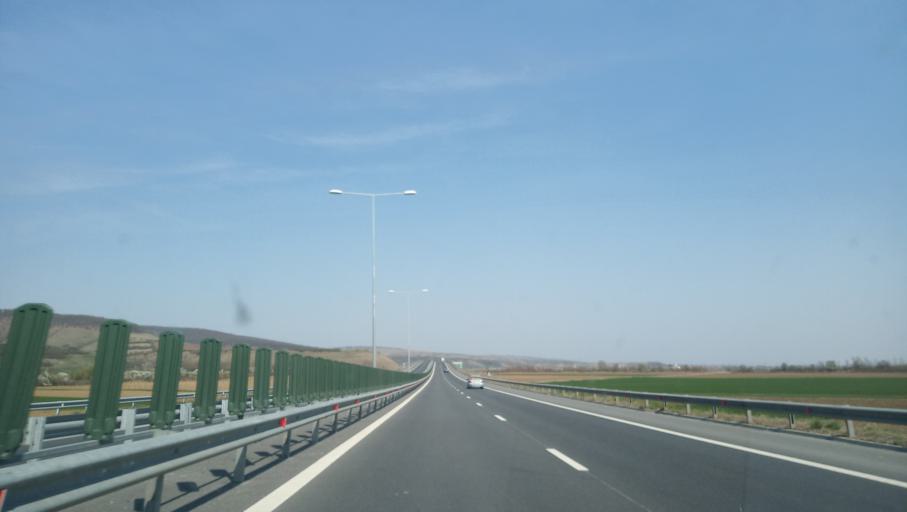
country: RO
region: Alba
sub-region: Comuna Miraslau
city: Miraslau
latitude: 46.3667
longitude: 23.7371
